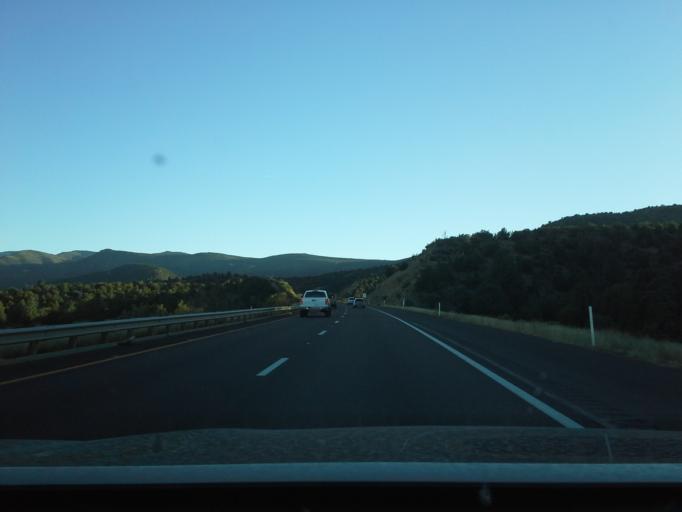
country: US
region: Arizona
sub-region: Yavapai County
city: Camp Verde
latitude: 34.5543
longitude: -111.9092
